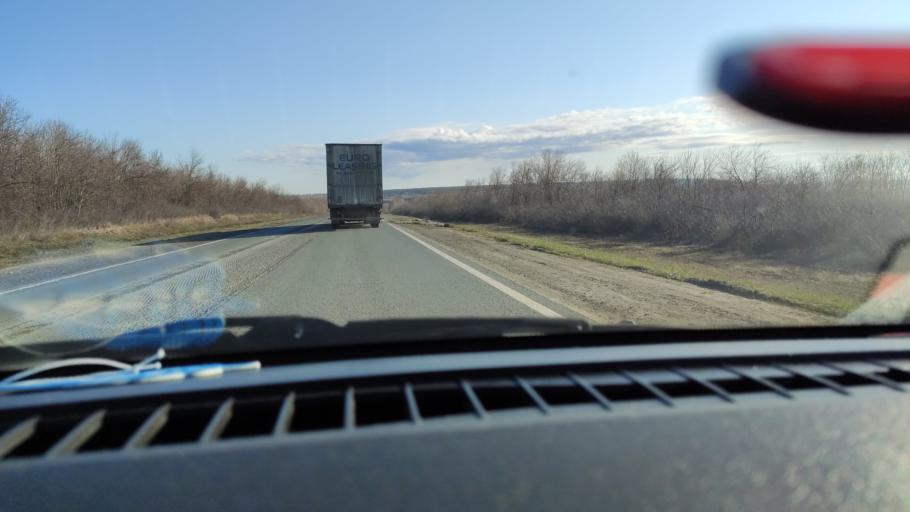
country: RU
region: Saratov
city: Dukhovnitskoye
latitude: 52.6873
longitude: 48.2398
